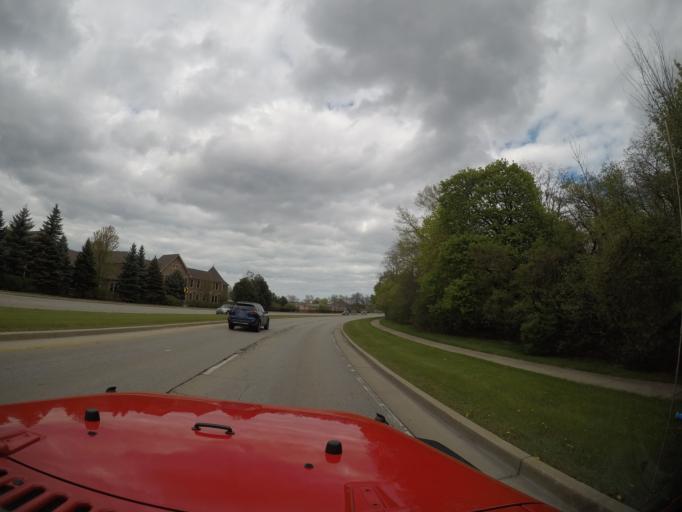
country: US
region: Illinois
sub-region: Cook County
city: Glenview
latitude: 42.0797
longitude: -87.8151
